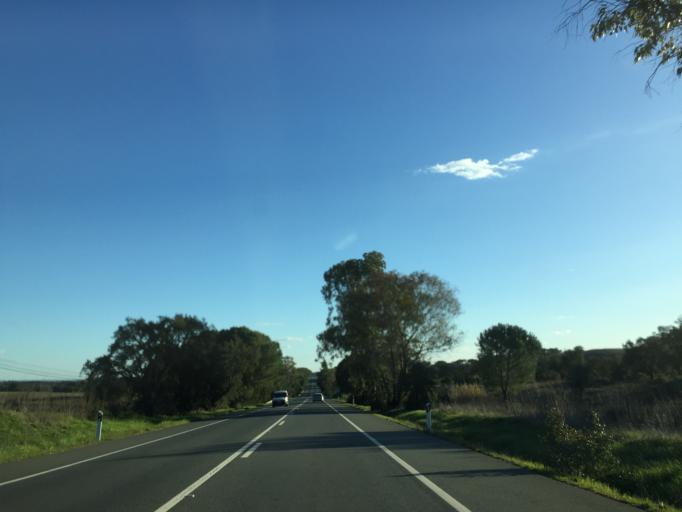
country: PT
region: Setubal
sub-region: Grandola
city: Grandola
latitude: 38.0916
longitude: -8.4182
